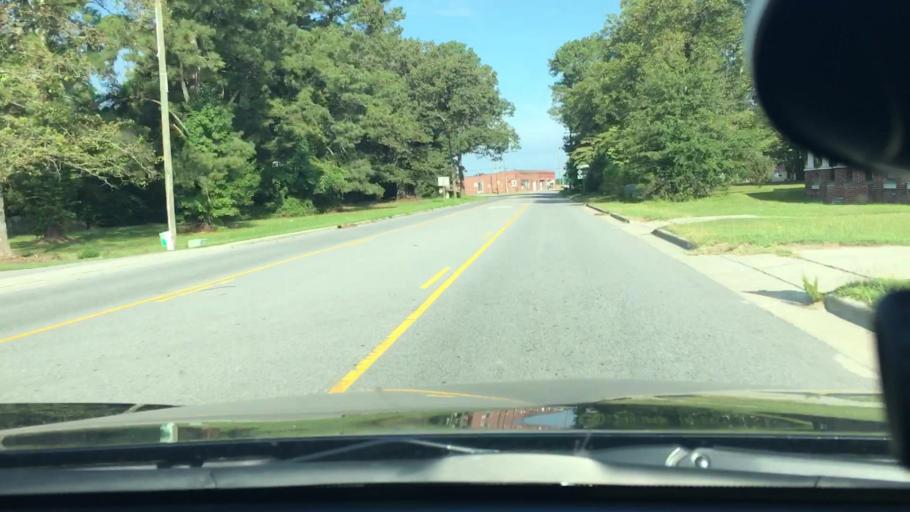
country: US
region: North Carolina
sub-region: Pitt County
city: Farmville
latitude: 35.6973
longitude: -77.5114
